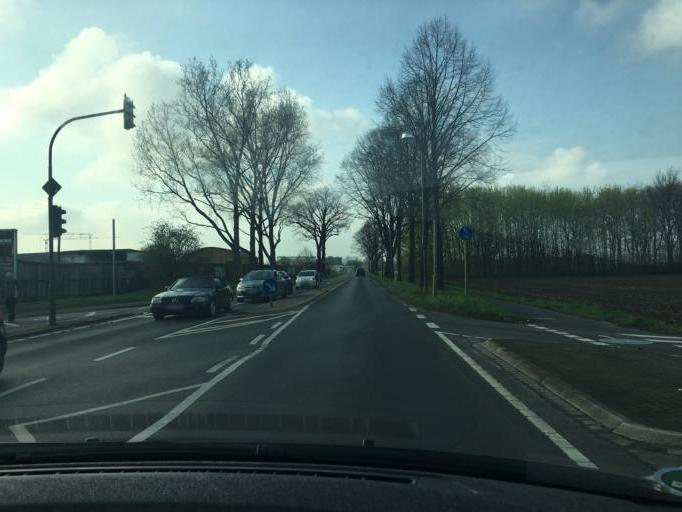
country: DE
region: North Rhine-Westphalia
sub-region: Regierungsbezirk Koln
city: Bonn
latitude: 50.7590
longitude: 7.0630
